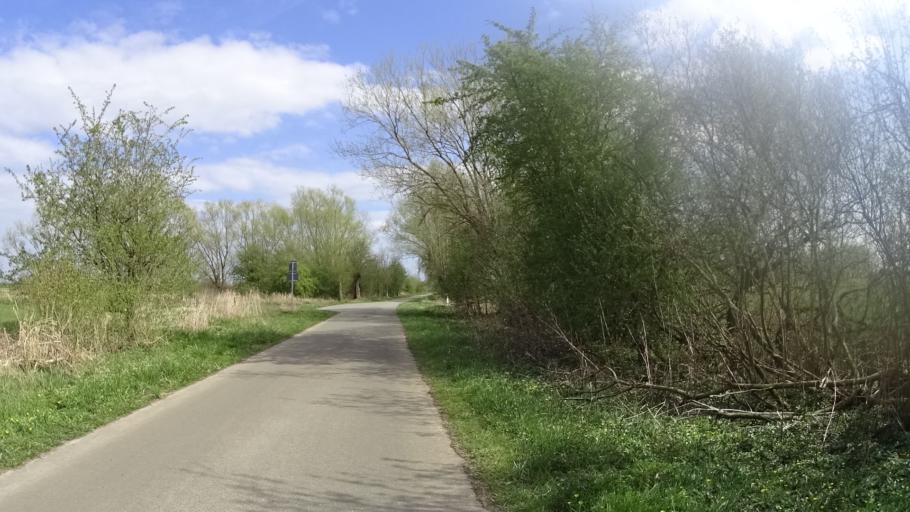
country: DE
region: Lower Saxony
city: Rhede
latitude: 53.0558
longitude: 7.3027
